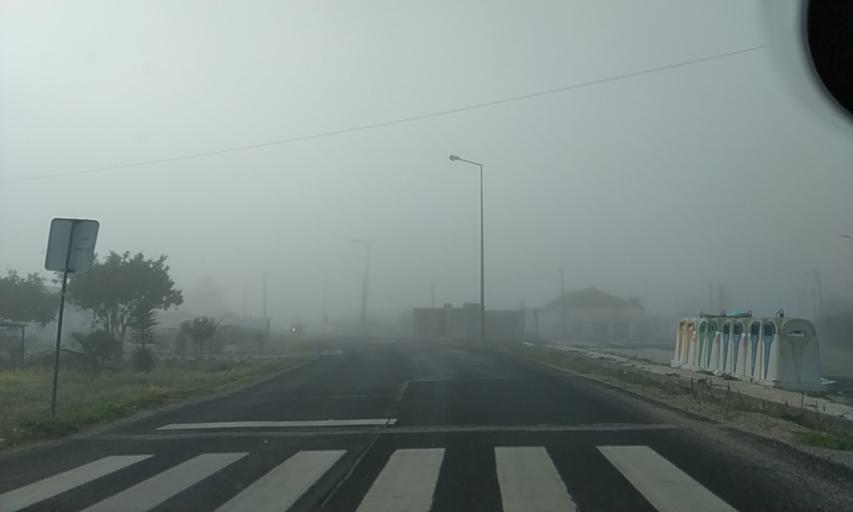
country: PT
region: Setubal
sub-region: Palmela
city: Pinhal Novo
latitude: 38.6103
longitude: -8.8863
